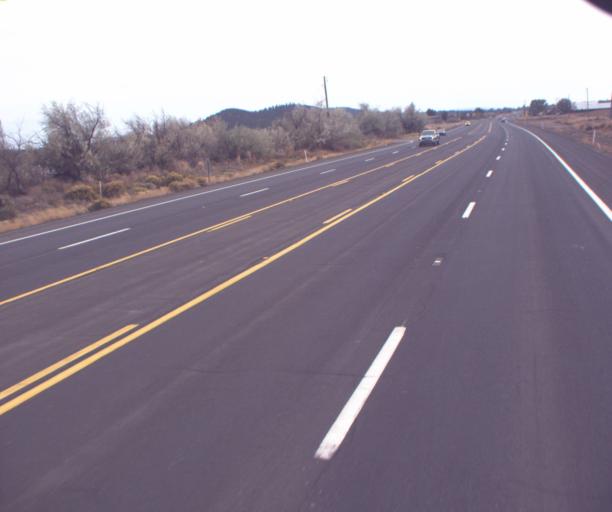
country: US
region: Arizona
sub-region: Coconino County
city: Flagstaff
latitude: 35.3169
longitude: -111.5428
